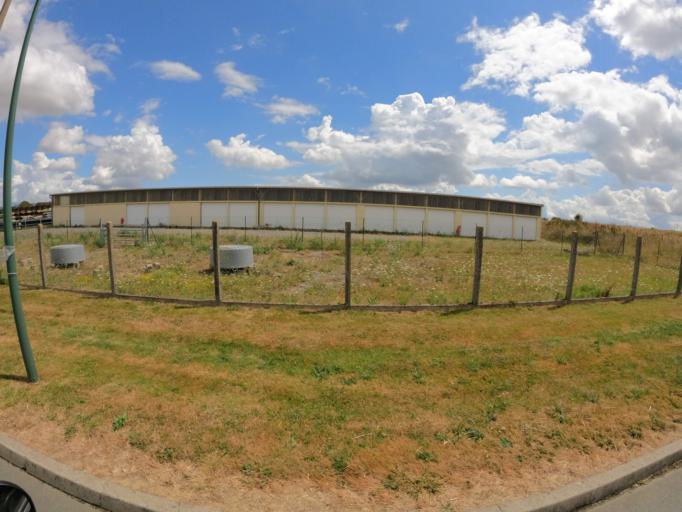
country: FR
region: Pays de la Loire
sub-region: Departement de Maine-et-Loire
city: Mire
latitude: 47.7513
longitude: -0.4989
